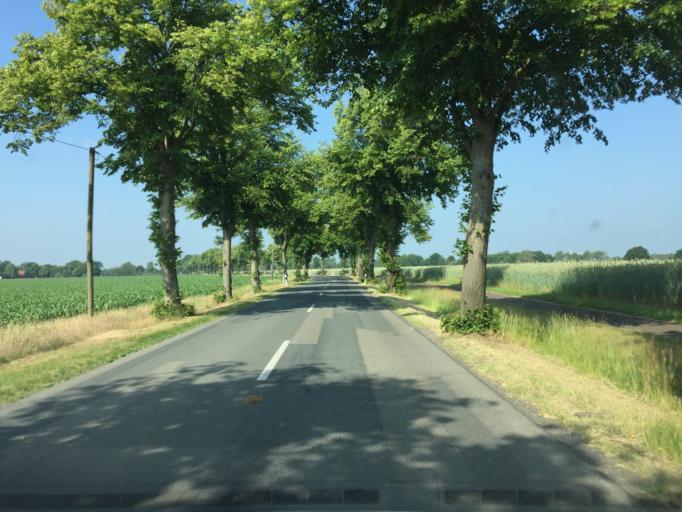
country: DE
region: Lower Saxony
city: Bahrenborstel
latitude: 52.5539
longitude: 8.7909
